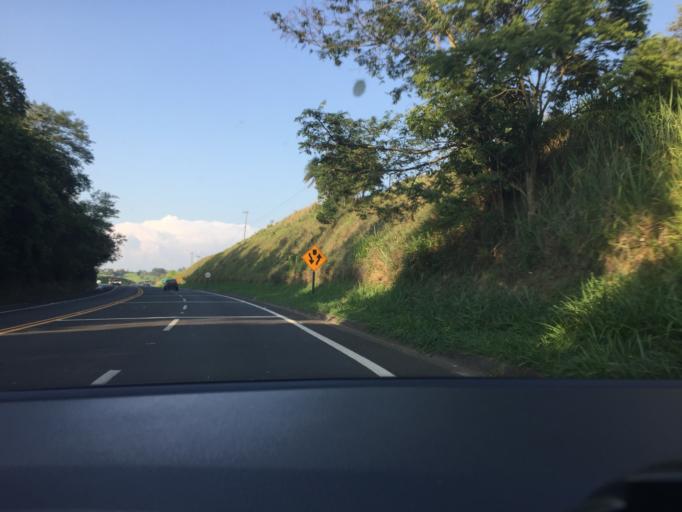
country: BR
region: Sao Paulo
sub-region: Louveira
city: Louveira
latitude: -23.0779
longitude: -46.9080
